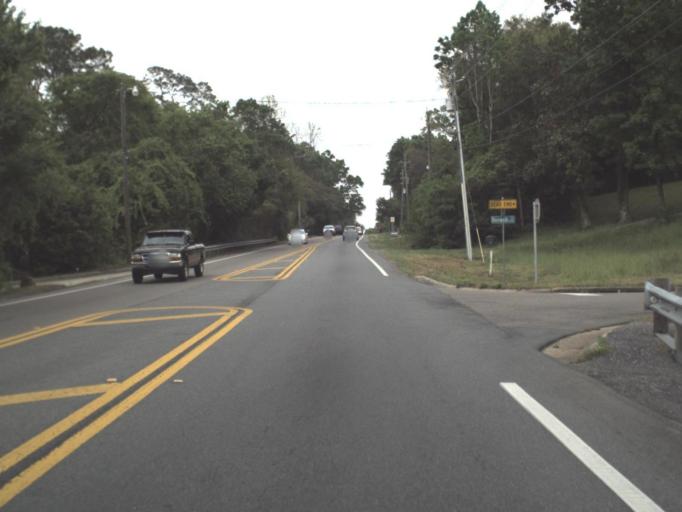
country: US
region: Florida
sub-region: Escambia County
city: Ferry Pass
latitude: 30.5245
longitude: -87.1834
